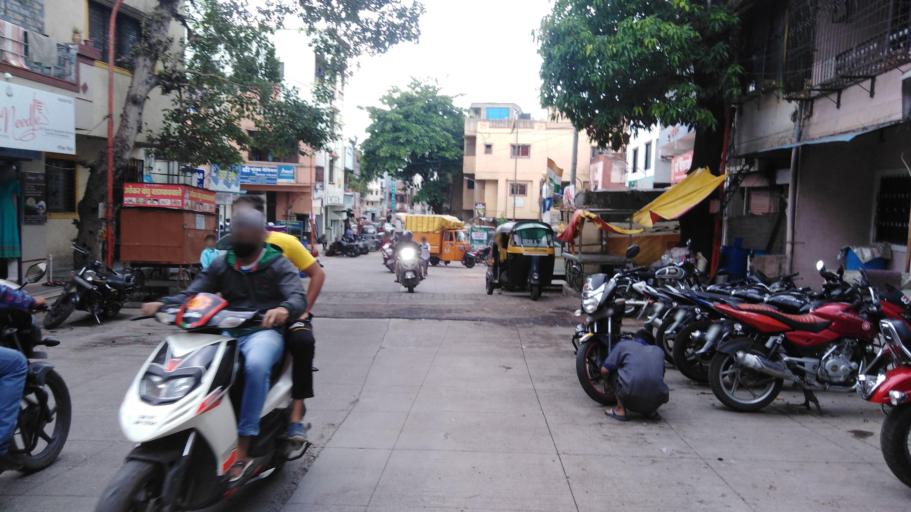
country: IN
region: Maharashtra
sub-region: Pune Division
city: Khadki
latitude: 18.5491
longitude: 73.8787
